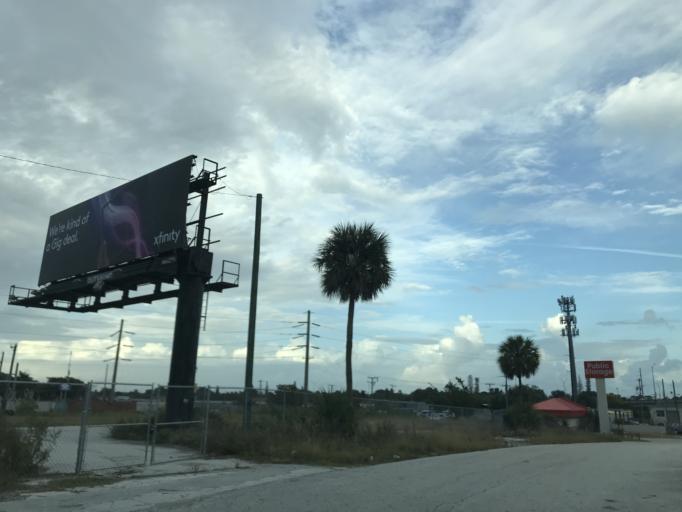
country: US
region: Florida
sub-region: Palm Beach County
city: Hypoluxo
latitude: 26.5726
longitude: -80.0722
